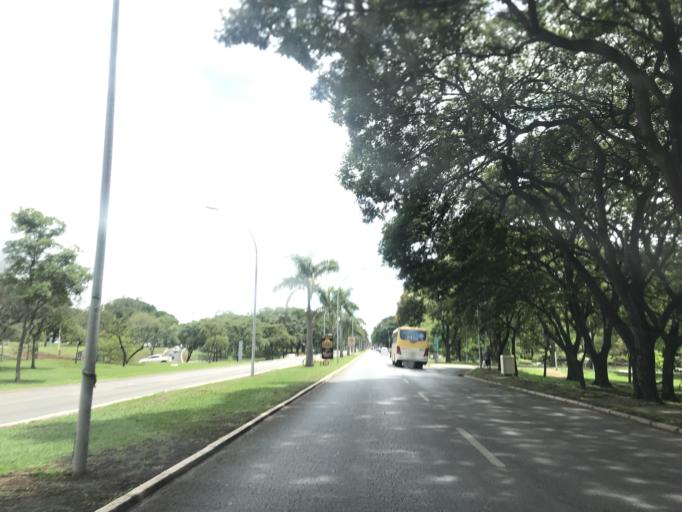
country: BR
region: Federal District
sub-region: Brasilia
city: Brasilia
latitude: -15.8302
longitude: -47.9179
